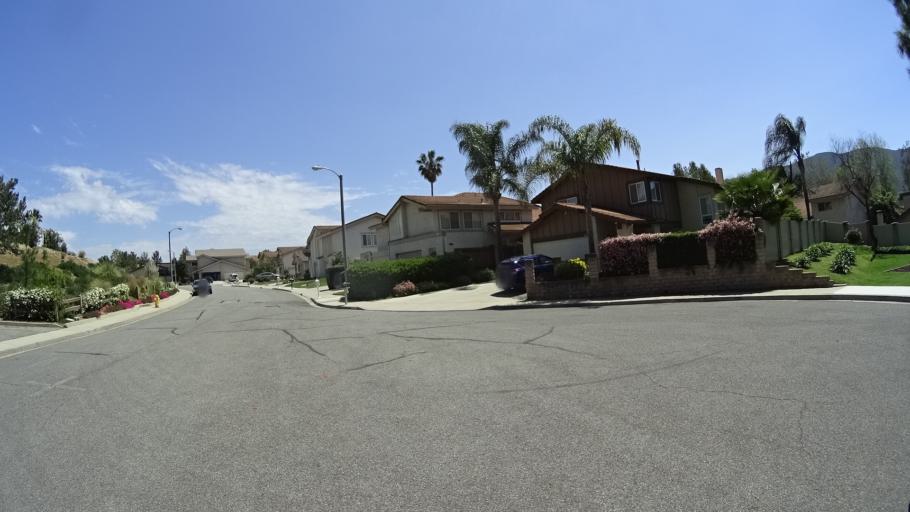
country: US
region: California
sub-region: Ventura County
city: Casa Conejo
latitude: 34.1814
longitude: -118.9187
